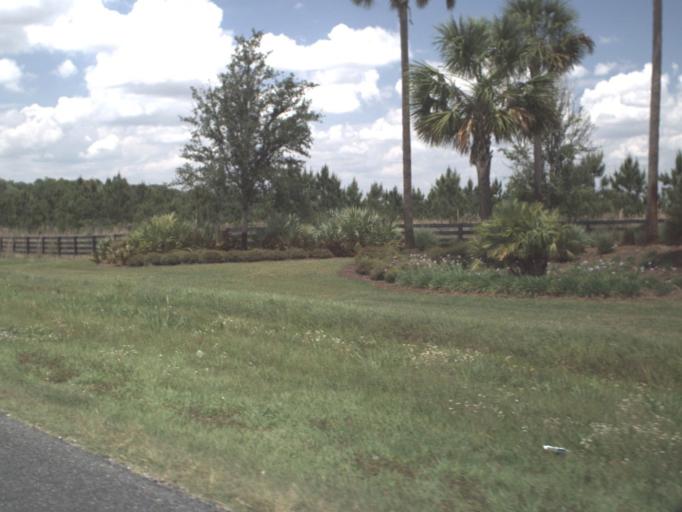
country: US
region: Florida
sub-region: Lake County
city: Fruitland Park
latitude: 28.8218
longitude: -81.9587
